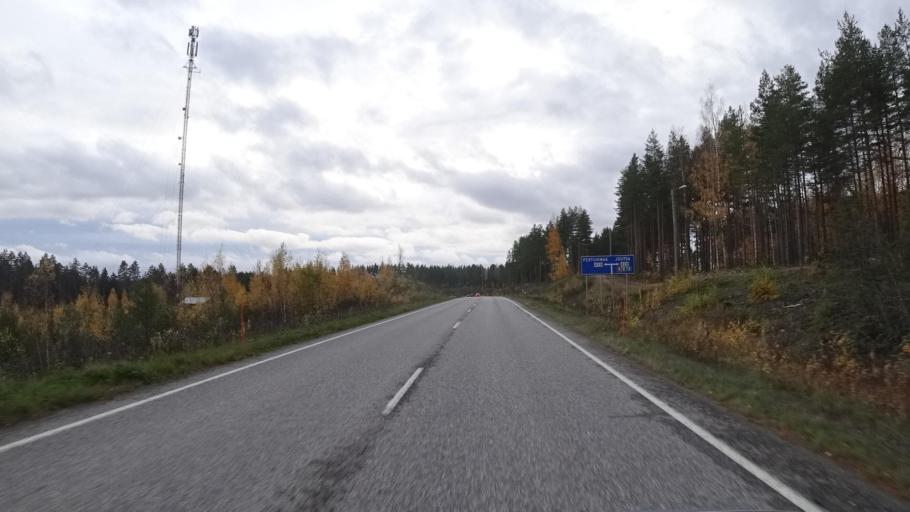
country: FI
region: Central Finland
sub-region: Joutsa
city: Joutsa
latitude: 61.7522
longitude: 26.1371
